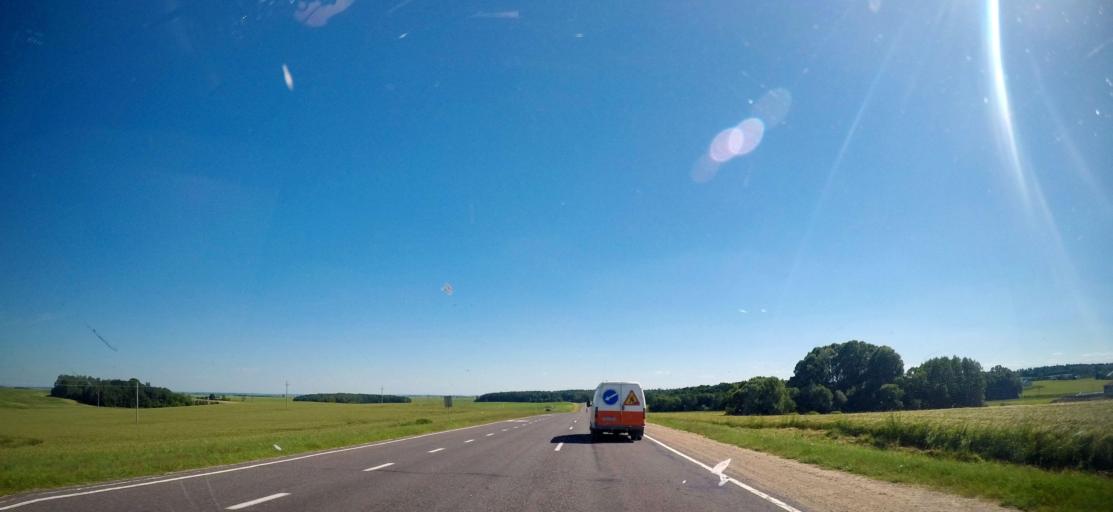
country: BY
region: Grodnenskaya
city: Indura
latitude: 53.5297
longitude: 23.8727
